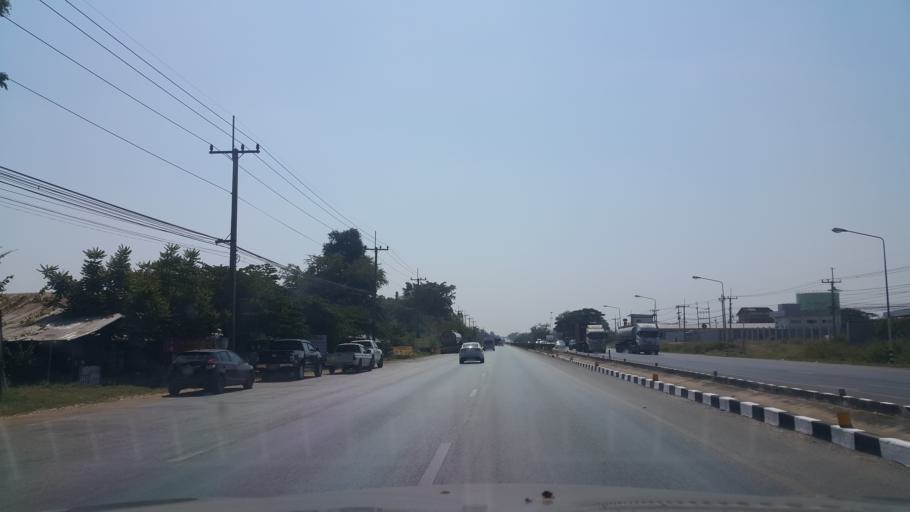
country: TH
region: Khon Kaen
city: Ban Haet
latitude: 16.1909
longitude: 102.7582
